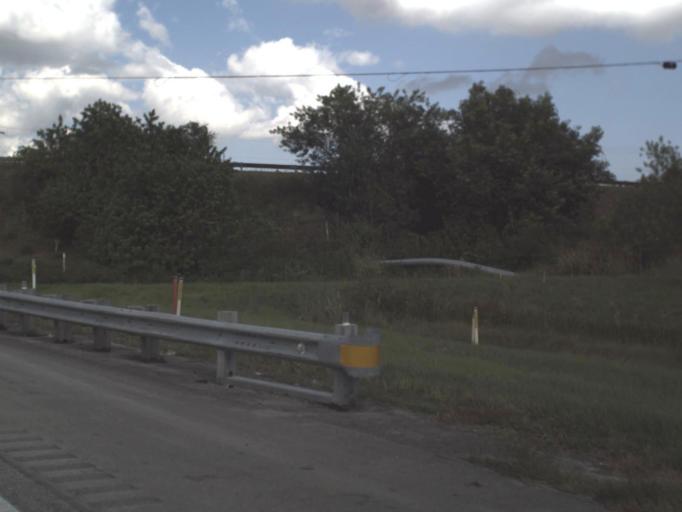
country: US
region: Florida
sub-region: Saint Lucie County
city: Fort Pierce South
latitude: 27.3738
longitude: -80.3836
